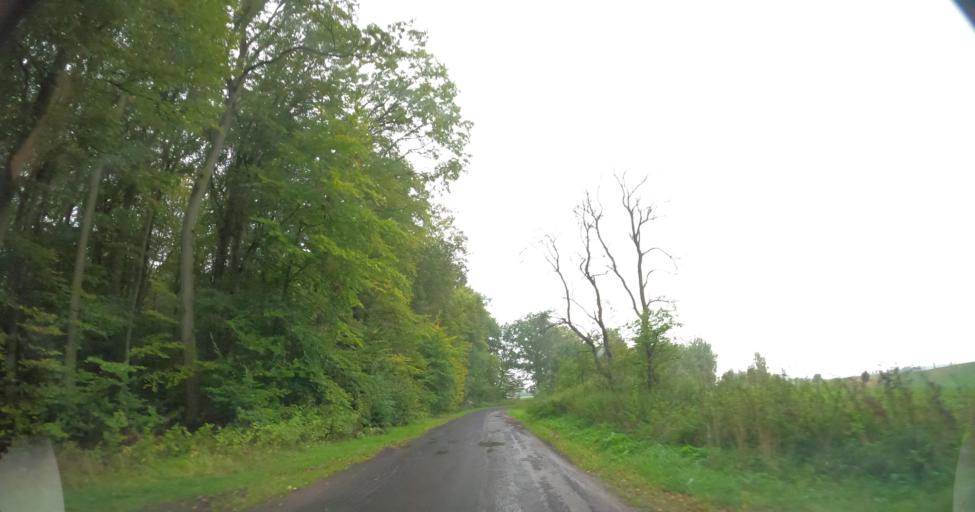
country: PL
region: West Pomeranian Voivodeship
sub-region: Powiat gryfinski
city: Banie
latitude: 53.0536
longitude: 14.7223
